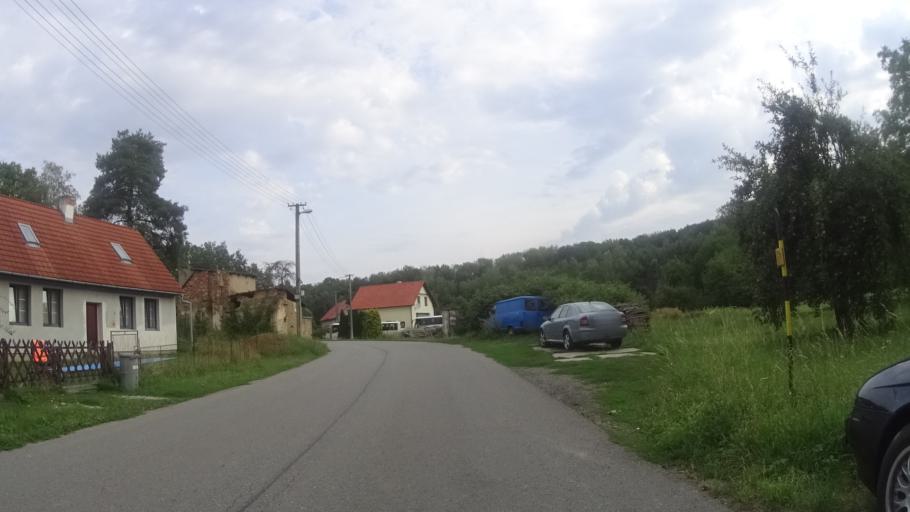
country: CZ
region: Zlin
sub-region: Okres Kromeriz
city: Kromeriz
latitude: 49.3244
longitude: 17.3878
